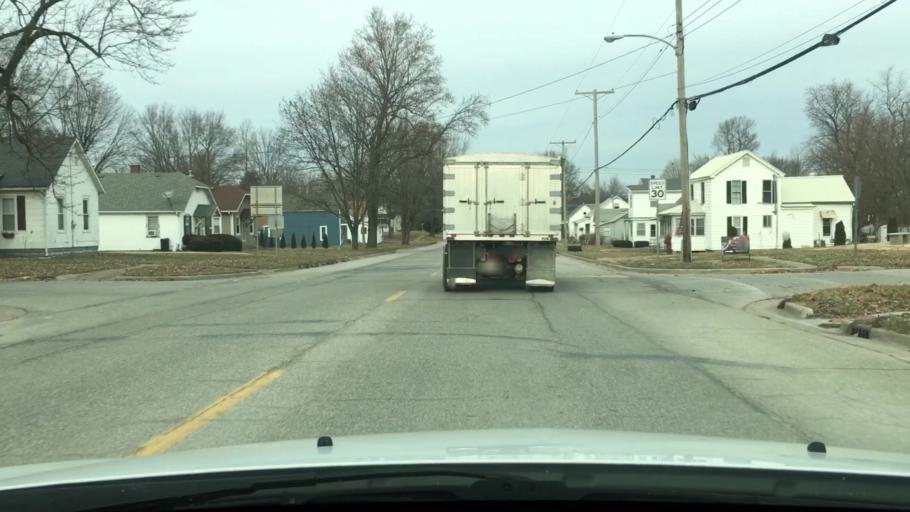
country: US
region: Illinois
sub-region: Pike County
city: Pittsfield
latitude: 39.6089
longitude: -90.8031
